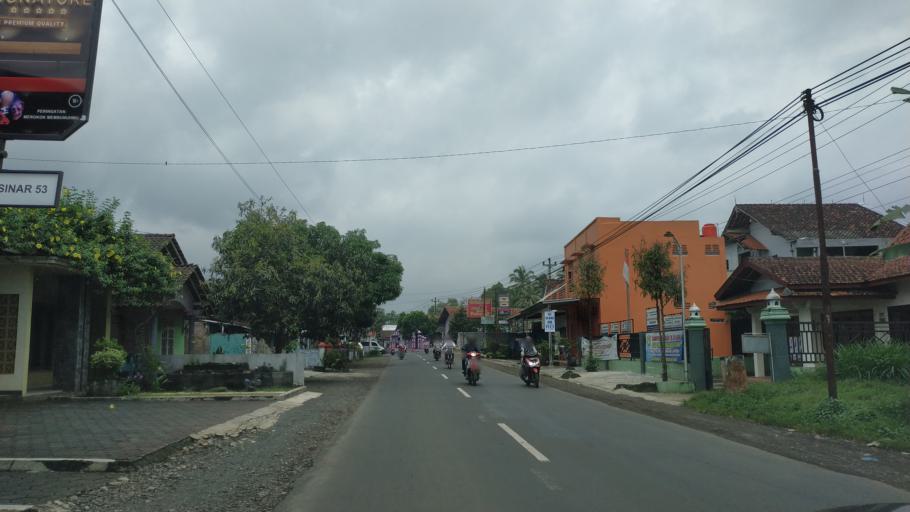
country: ID
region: Central Java
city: Weleri
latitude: -7.0810
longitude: 110.0429
